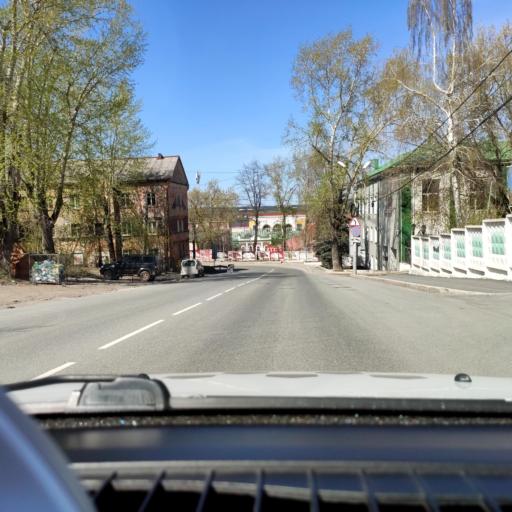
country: RU
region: Perm
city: Perm
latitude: 58.0185
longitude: 56.2537
